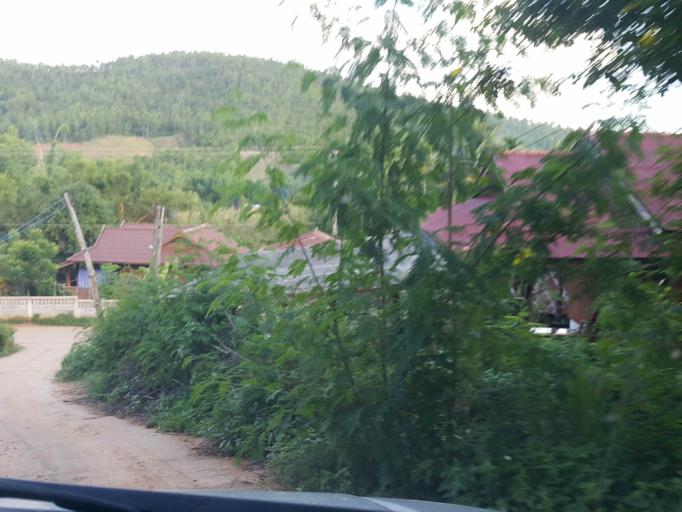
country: TH
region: Chiang Mai
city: Mae Chaem
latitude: 18.4905
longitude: 98.3864
